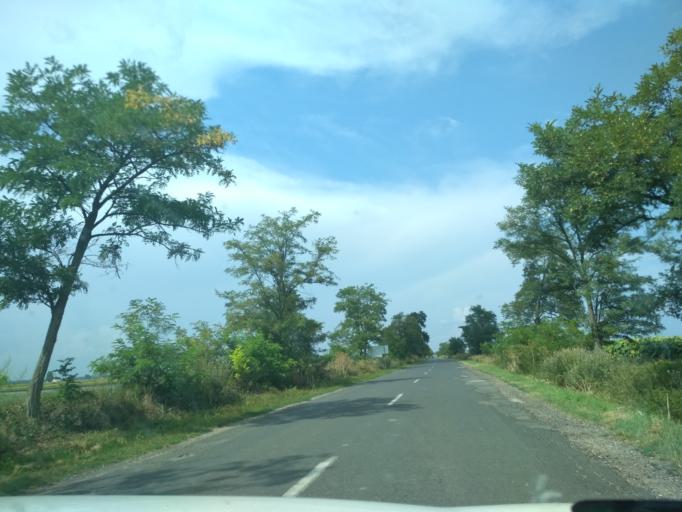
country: HU
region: Jasz-Nagykun-Szolnok
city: Tiszaszolos
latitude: 47.5359
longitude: 20.7151
